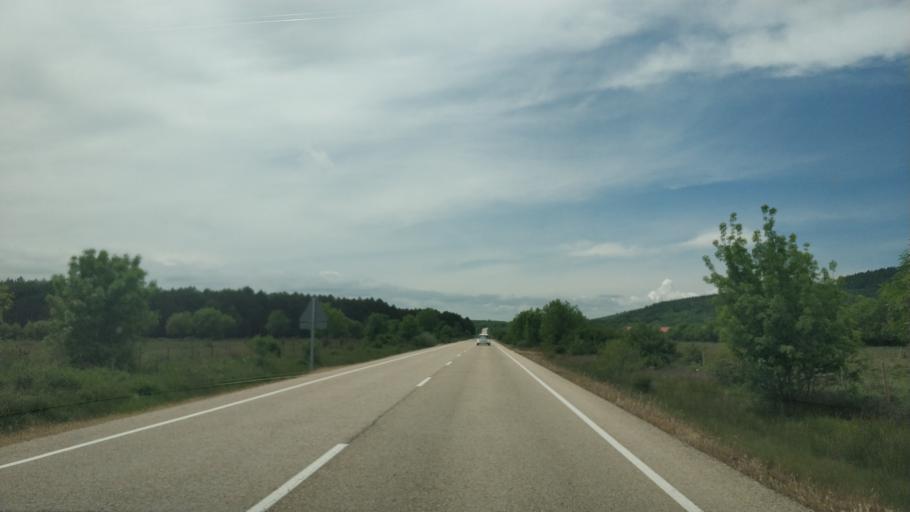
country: ES
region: Castille and Leon
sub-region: Provincia de Soria
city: Sotillo del Rincon
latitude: 41.8938
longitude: -2.6708
